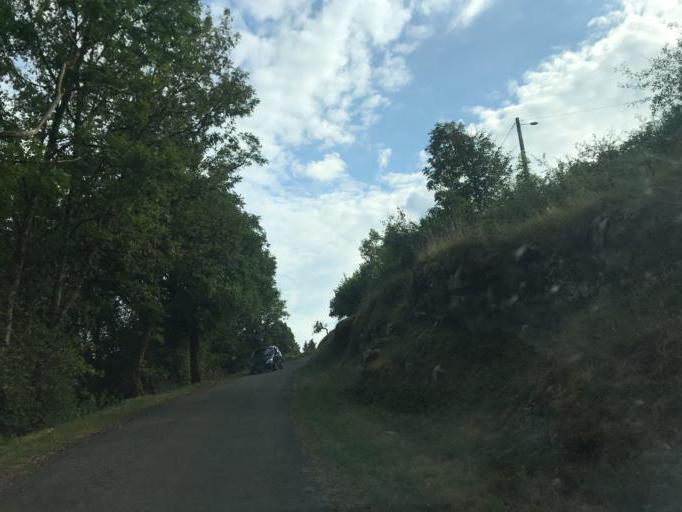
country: FR
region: Franche-Comte
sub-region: Departement du Jura
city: Saint-Lupicin
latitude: 46.4297
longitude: 5.8057
